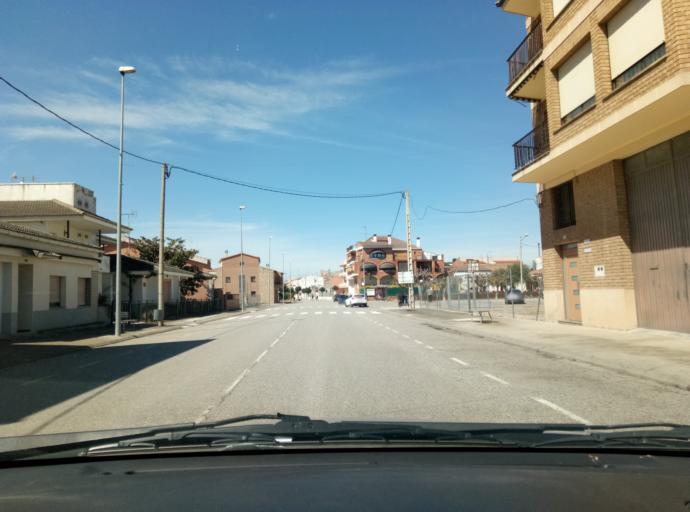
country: ES
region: Catalonia
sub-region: Provincia de Lleida
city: Vinaixa
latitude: 41.4237
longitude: 0.9416
